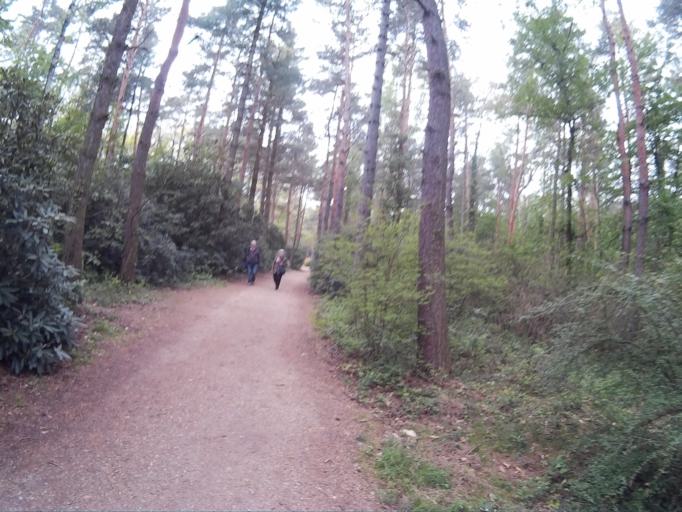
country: HU
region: Vas
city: Vasvar
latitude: 47.0732
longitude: 16.8919
